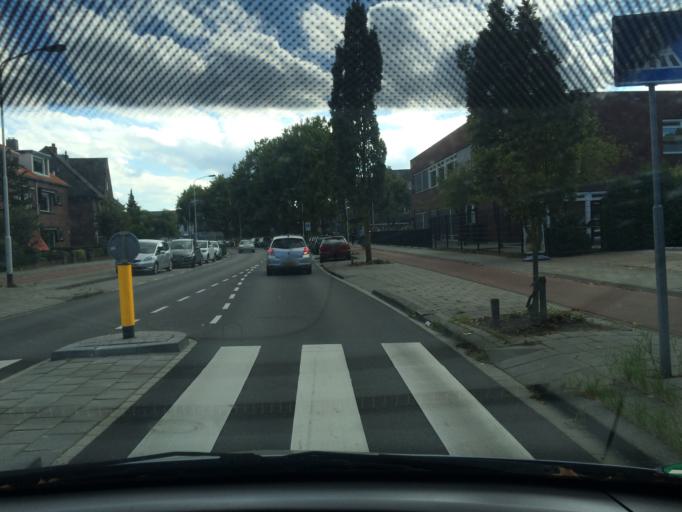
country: NL
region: North Brabant
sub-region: Gemeente Breda
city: Breda
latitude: 51.5999
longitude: 4.7787
